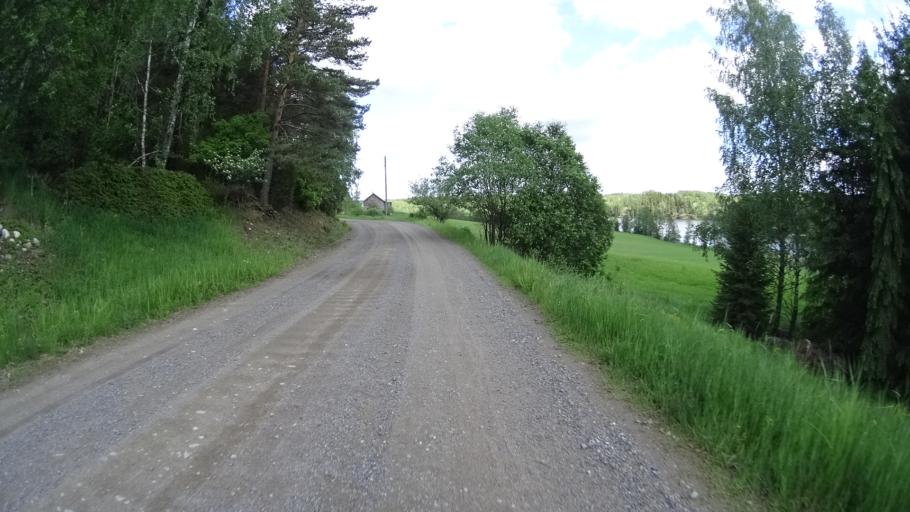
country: FI
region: Uusimaa
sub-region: Raaseporin
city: Pohja
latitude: 60.1211
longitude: 23.5950
